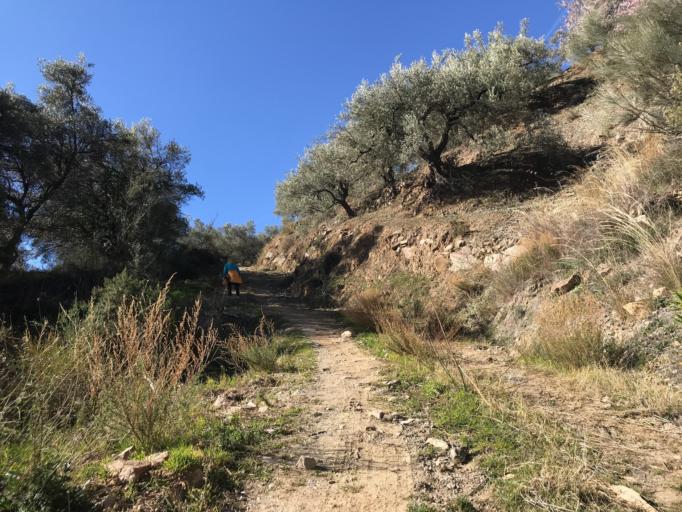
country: ES
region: Andalusia
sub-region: Provincia de Malaga
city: Canillas de Albaida
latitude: 36.8527
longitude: -3.9865
